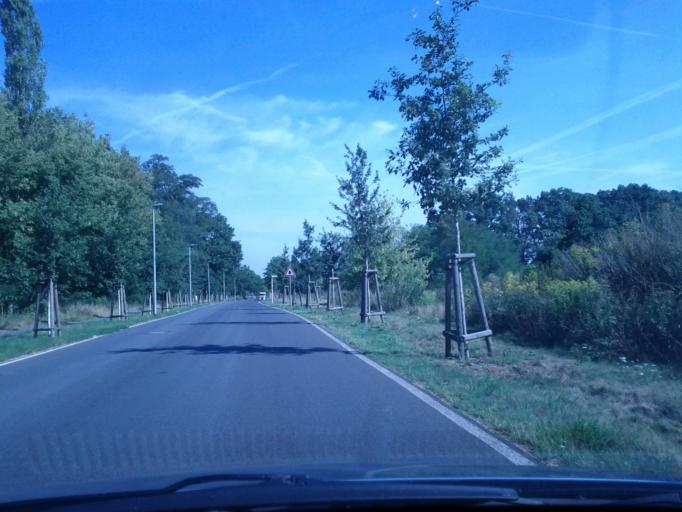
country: DE
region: Brandenburg
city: Schoneiche
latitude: 52.4927
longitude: 13.7022
